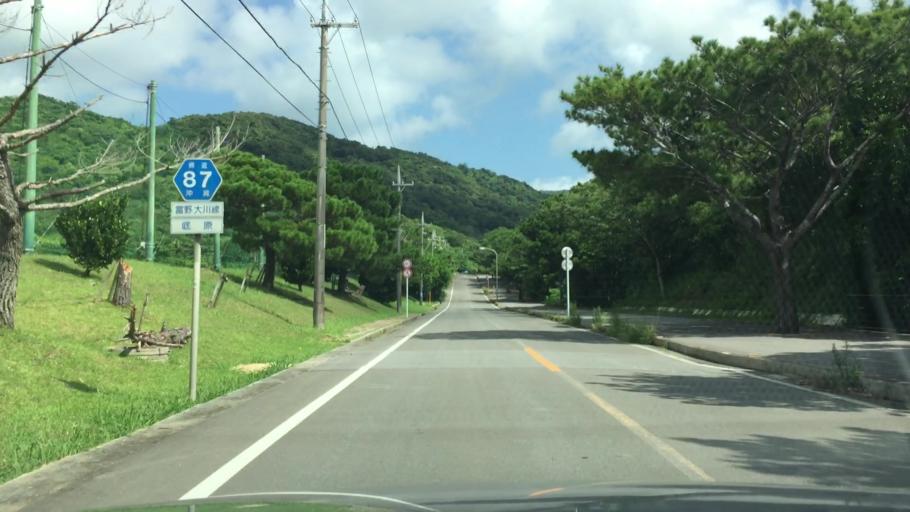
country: JP
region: Okinawa
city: Ishigaki
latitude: 24.4243
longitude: 124.2126
